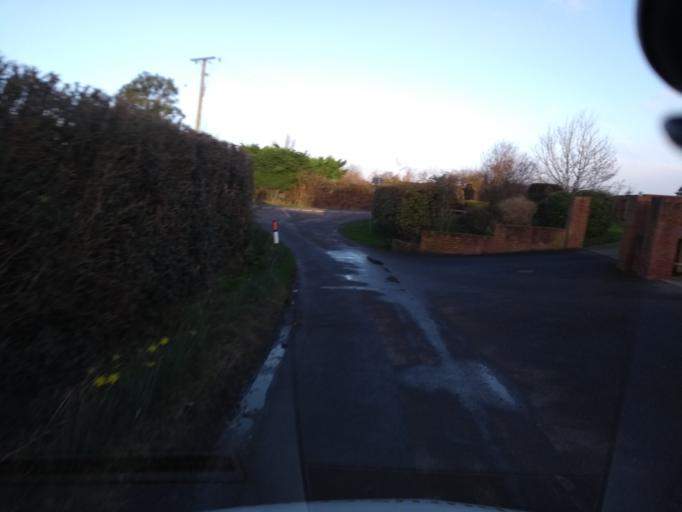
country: GB
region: England
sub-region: Somerset
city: Bridgwater
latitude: 51.1479
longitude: -3.0083
